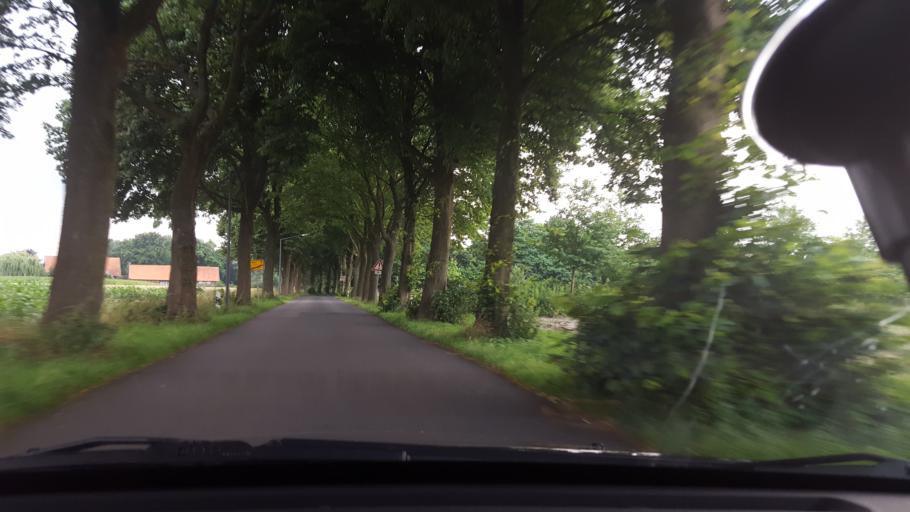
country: DE
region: North Rhine-Westphalia
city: Herten
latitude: 51.6254
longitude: 7.1419
